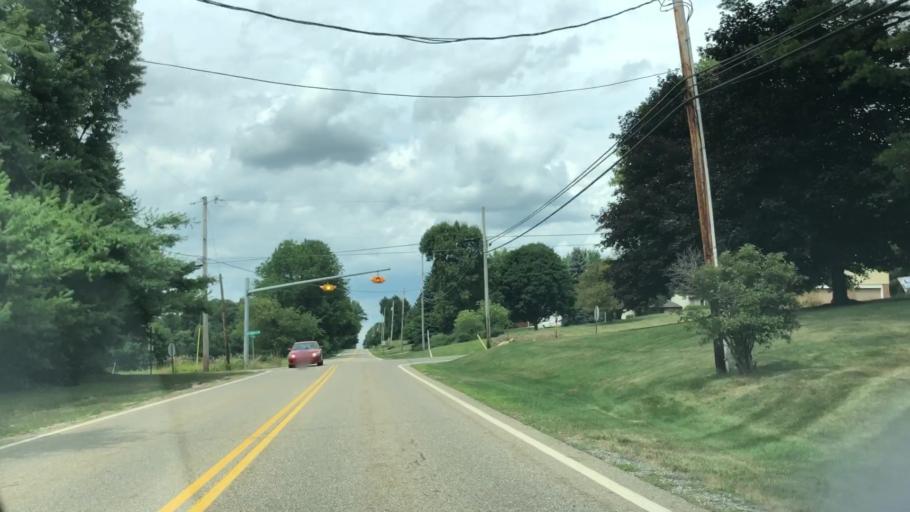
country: US
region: Ohio
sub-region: Summit County
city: Greensburg
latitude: 40.8850
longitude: -81.4598
